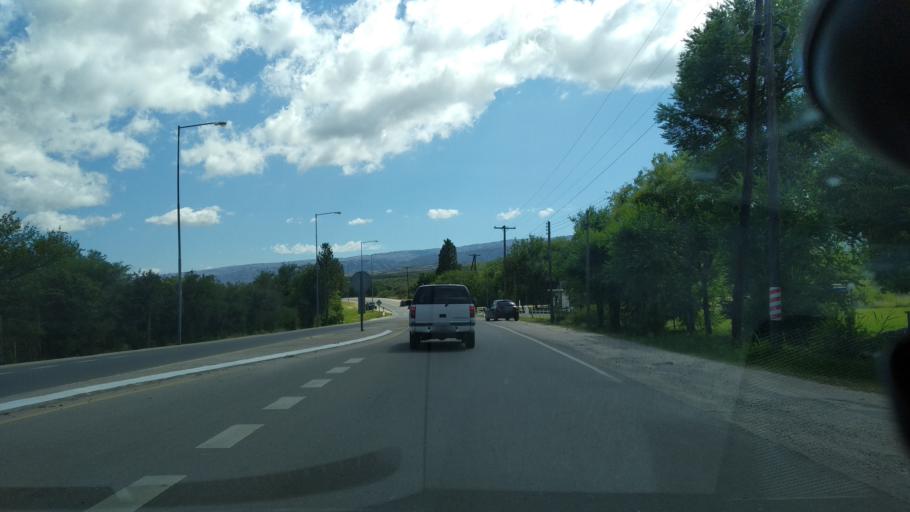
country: AR
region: Cordoba
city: Mina Clavero
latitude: -31.7915
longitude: -64.9998
